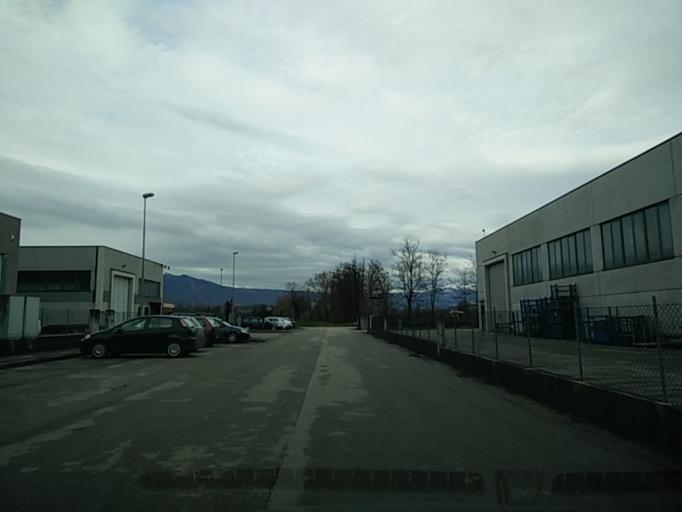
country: IT
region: Veneto
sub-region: Provincia di Treviso
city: Ca' Rainati
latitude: 45.7623
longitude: 11.8667
